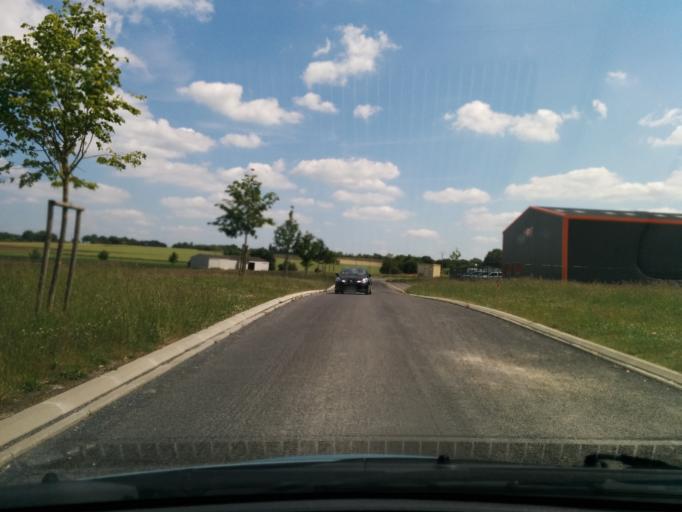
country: FR
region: Ile-de-France
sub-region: Departement des Yvelines
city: Freneuse
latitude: 49.0365
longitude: 1.6043
